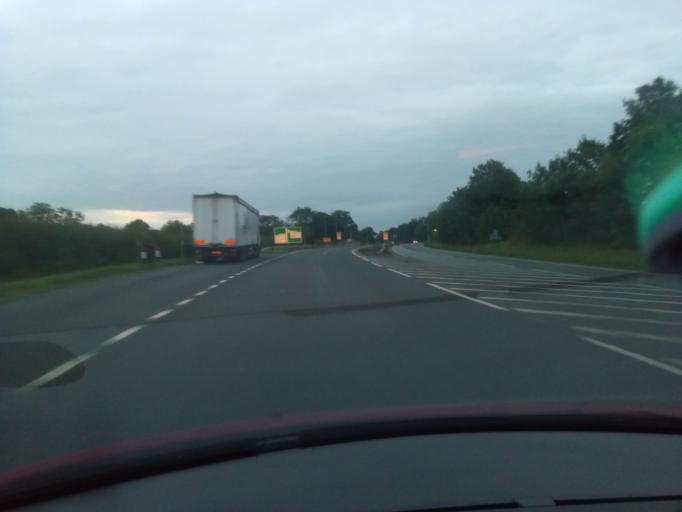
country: GB
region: England
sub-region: Northumberland
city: Warden
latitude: 54.9830
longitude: -2.1355
